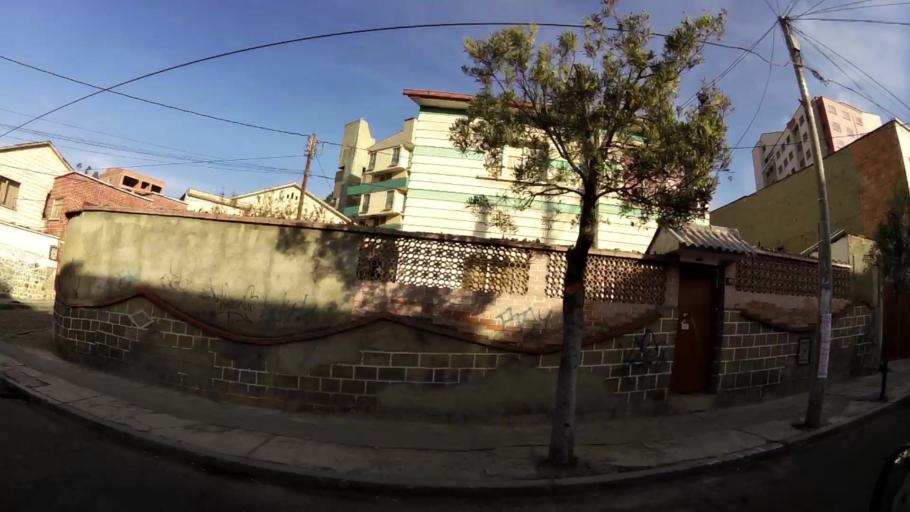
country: BO
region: La Paz
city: La Paz
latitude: -16.4862
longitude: -68.1229
